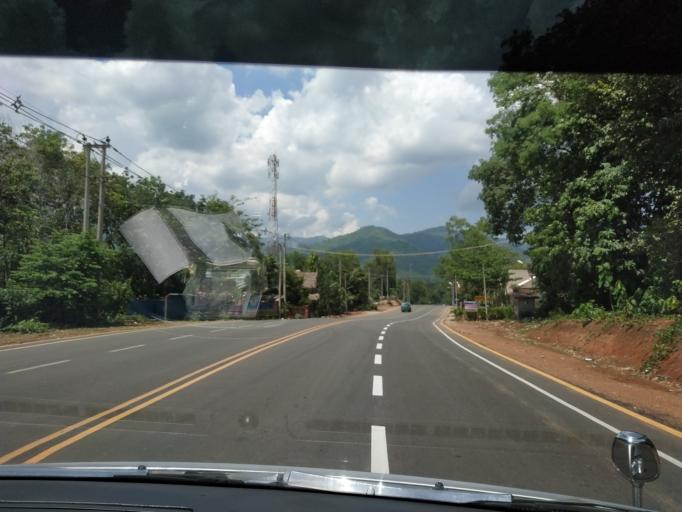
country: MM
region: Mon
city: Kyaikto
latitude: 17.3951
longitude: 97.0734
